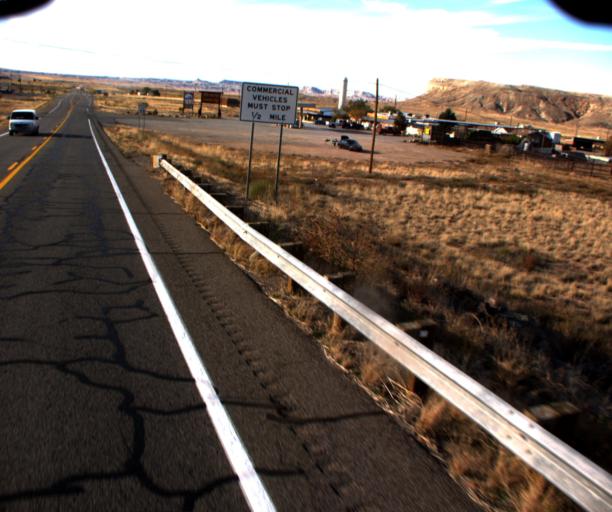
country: US
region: New Mexico
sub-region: San Juan County
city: Shiprock
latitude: 36.9186
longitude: -109.0832
